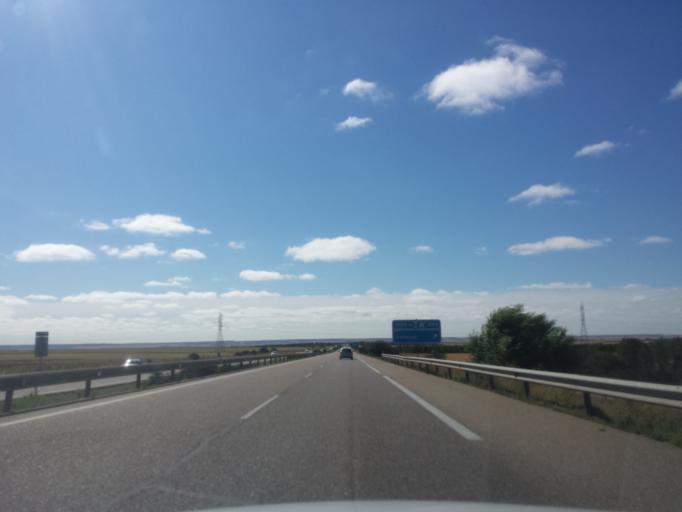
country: ES
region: Castille and Leon
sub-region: Provincia de Zamora
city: Quintanilla del Monte
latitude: 41.8097
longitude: -5.3563
